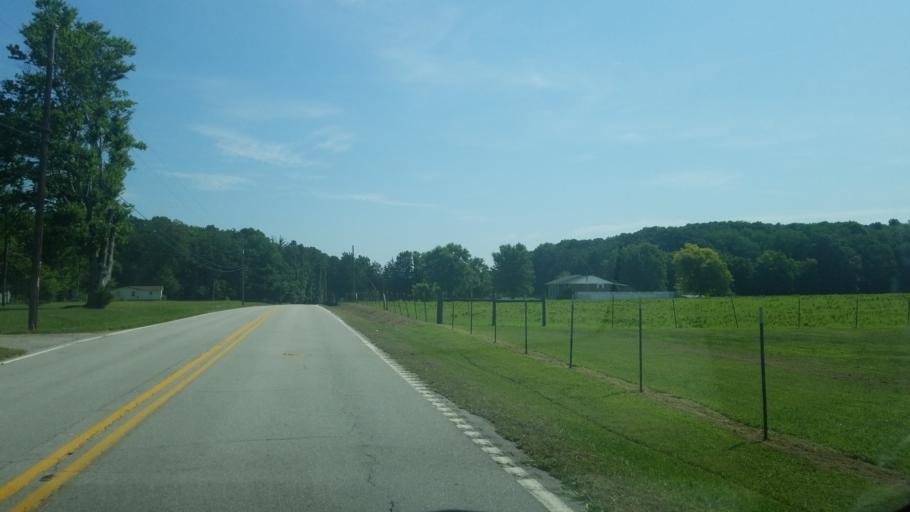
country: US
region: Tennessee
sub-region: Hamilton County
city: Sale Creek
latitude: 35.3479
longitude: -84.9990
